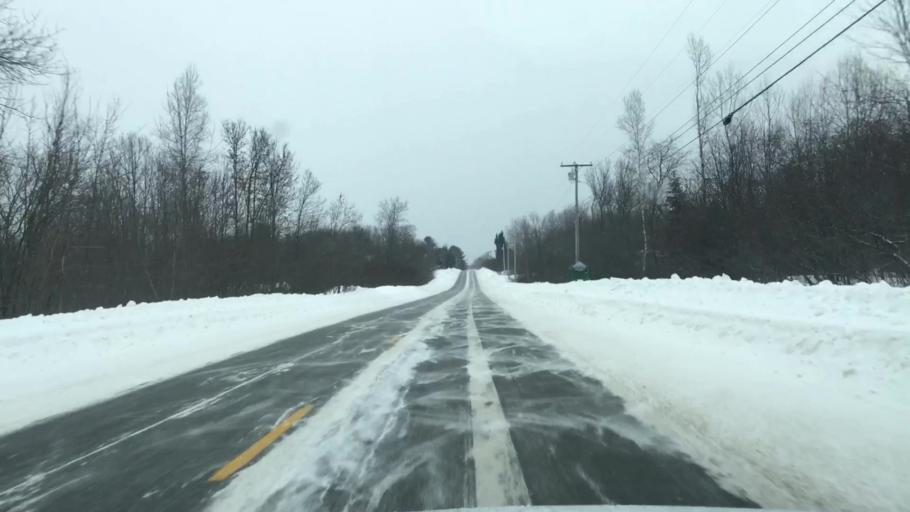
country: US
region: Maine
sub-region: Penobscot County
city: Lincoln
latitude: 45.4378
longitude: -68.4407
